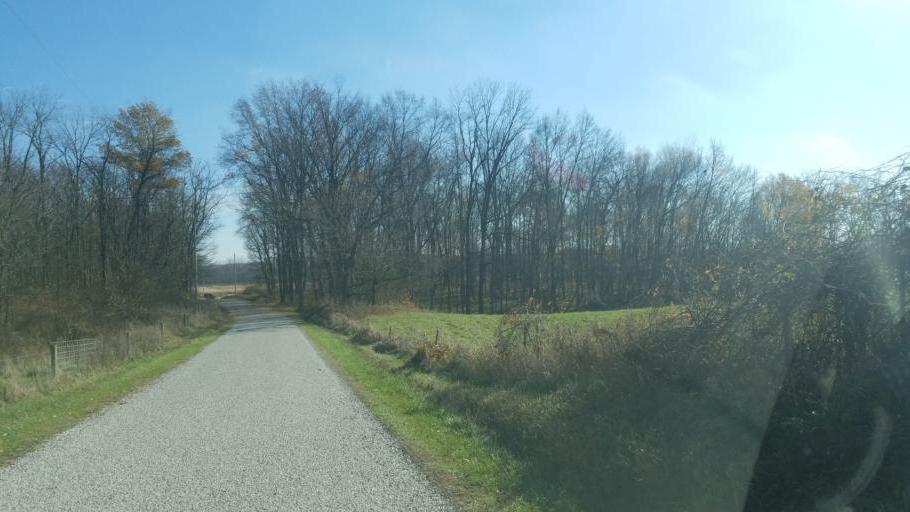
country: US
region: Ohio
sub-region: Ashland County
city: Ashland
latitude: 40.9212
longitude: -82.3016
